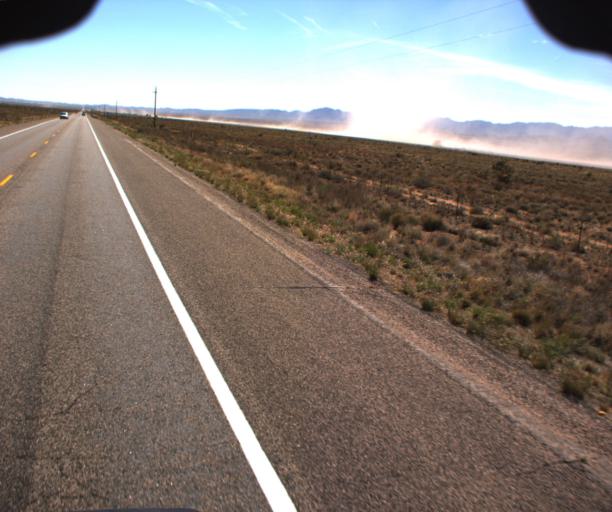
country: US
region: Arizona
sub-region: Mohave County
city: New Kingman-Butler
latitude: 35.3707
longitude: -113.8638
